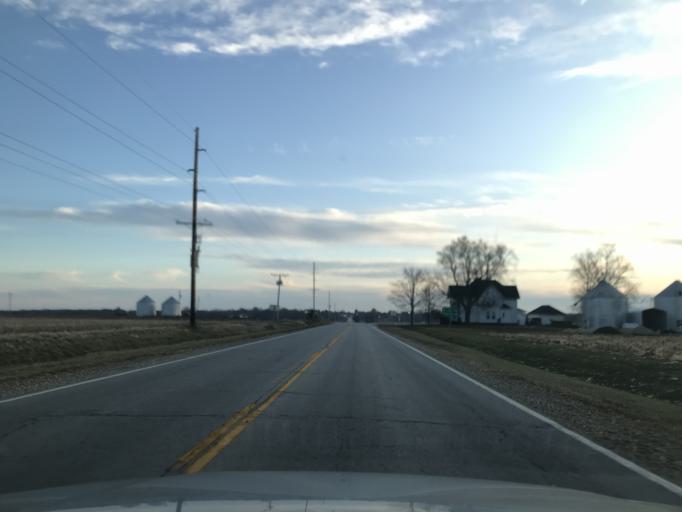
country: US
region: Illinois
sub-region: Warren County
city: Monmouth
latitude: 41.0260
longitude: -90.7460
